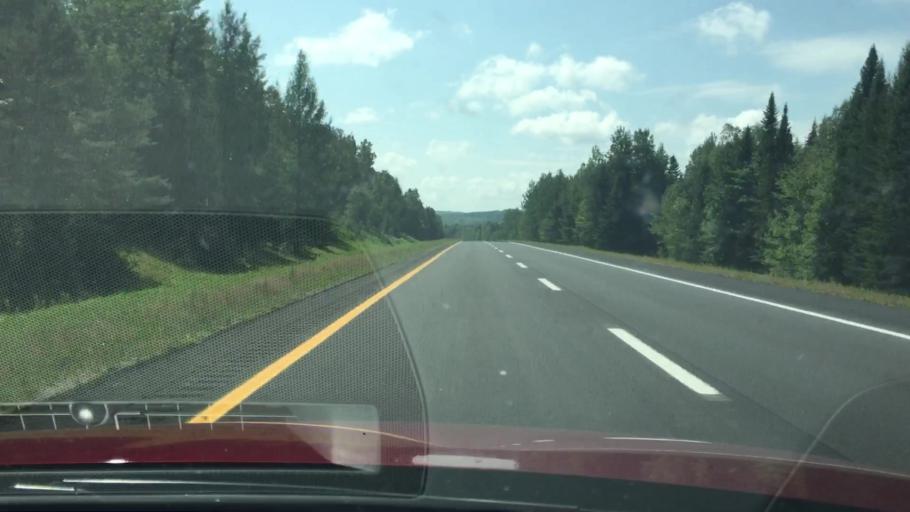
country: US
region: Maine
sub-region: Penobscot County
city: Patten
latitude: 45.8997
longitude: -68.3925
